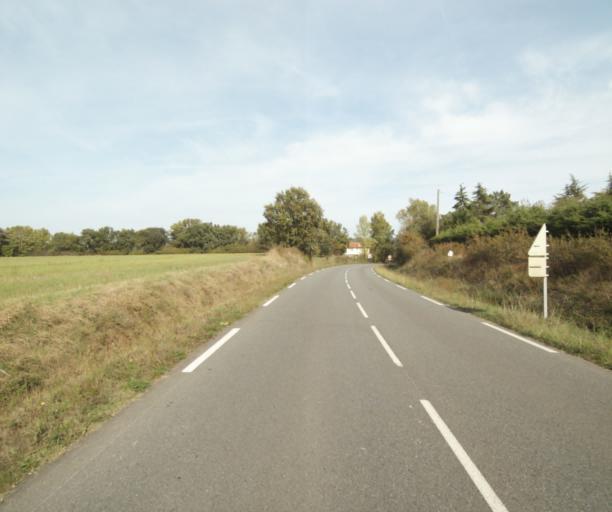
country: FR
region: Midi-Pyrenees
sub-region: Departement du Tarn-et-Garonne
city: Orgueil
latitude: 43.9128
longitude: 1.3946
